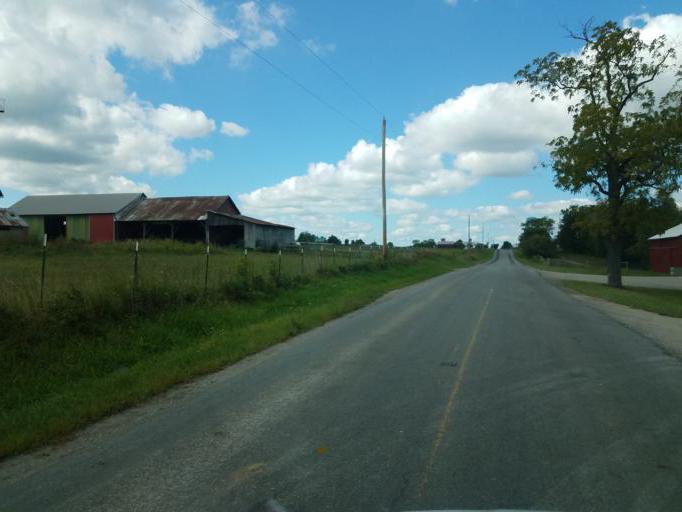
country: US
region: Ohio
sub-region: Wayne County
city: West Salem
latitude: 41.0421
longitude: -82.1053
